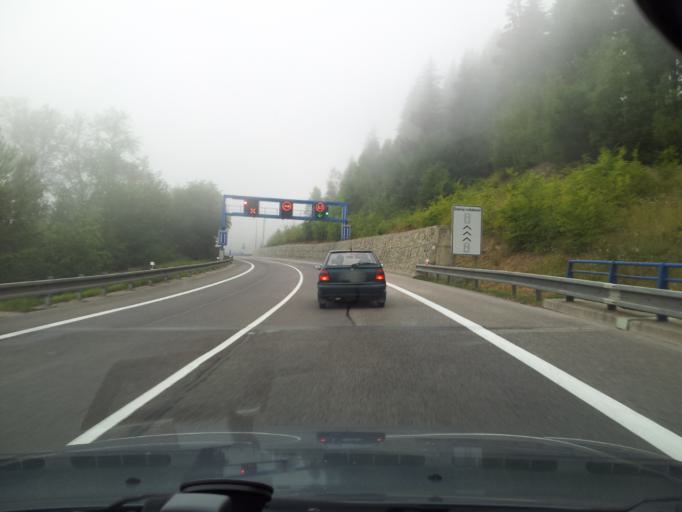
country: SK
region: Zilinsky
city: Cadca
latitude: 49.4308
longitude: 18.8127
